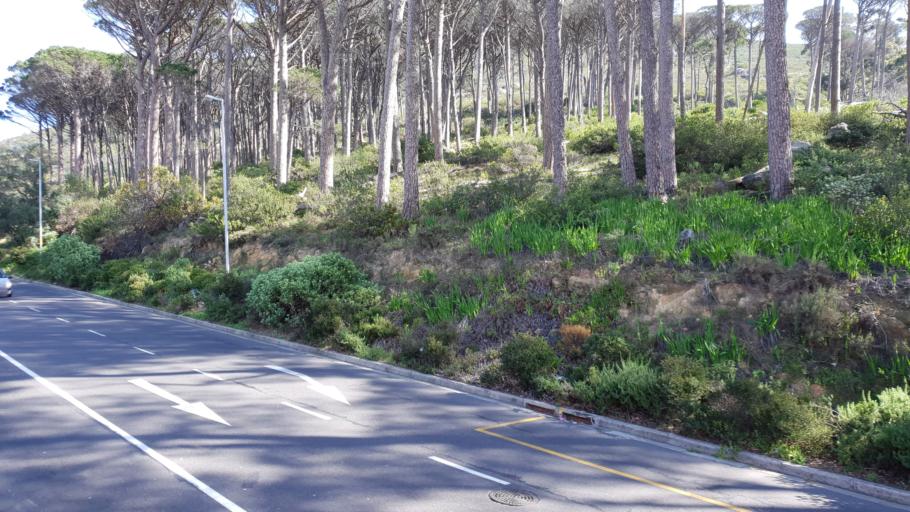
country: ZA
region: Western Cape
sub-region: City of Cape Town
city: Cape Town
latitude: -33.9363
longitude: 18.4005
